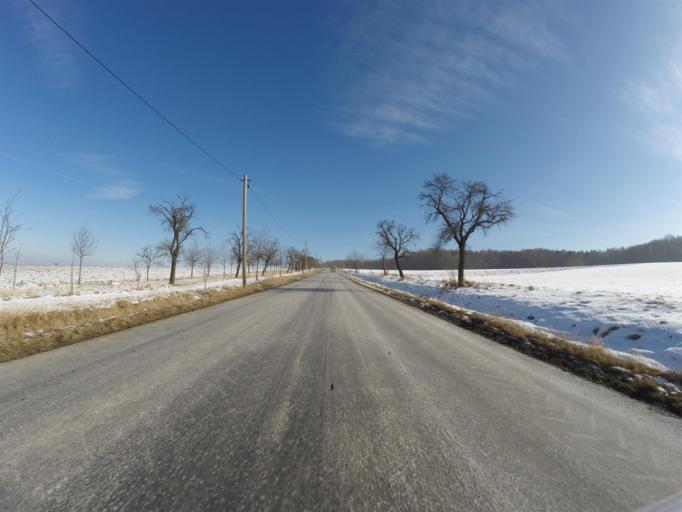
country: DE
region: Thuringia
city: Dobritschen
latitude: 50.9177
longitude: 11.4810
